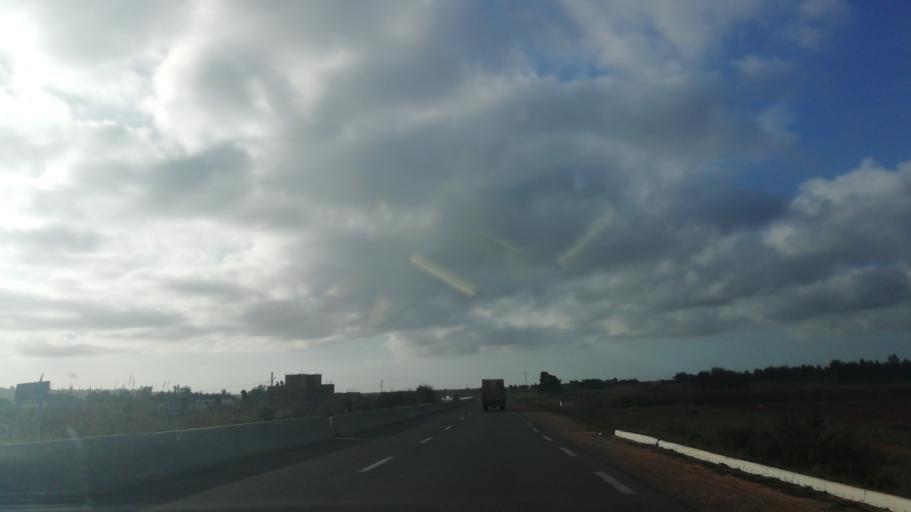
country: DZ
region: Mostaganem
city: Mostaganem
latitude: 36.1025
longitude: 0.2657
